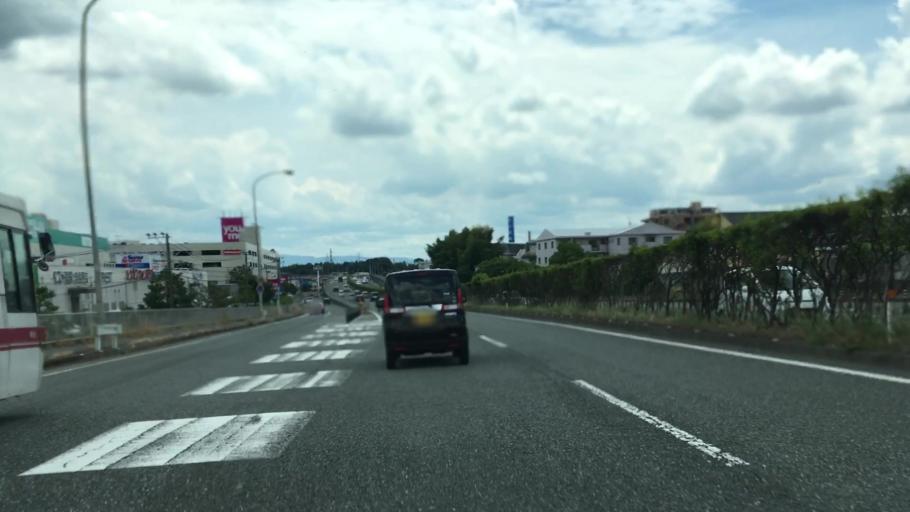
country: JP
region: Fukuoka
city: Chikushino-shi
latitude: 33.4870
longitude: 130.5361
